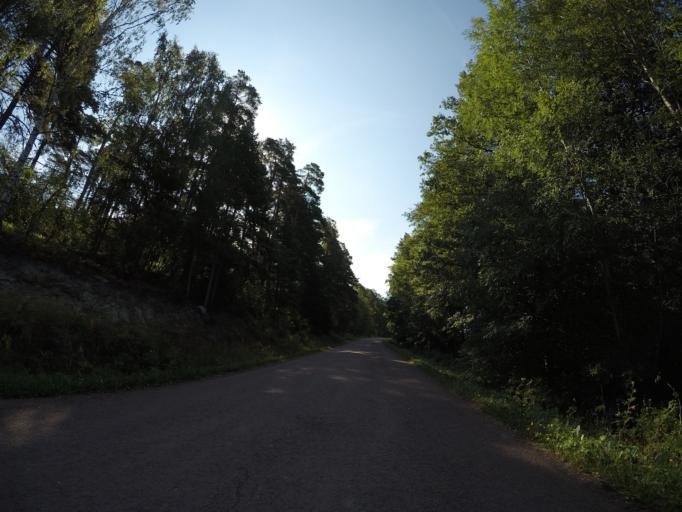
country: AX
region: Alands landsbygd
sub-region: Finstroem
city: Finstroem
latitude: 60.2691
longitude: 19.9272
